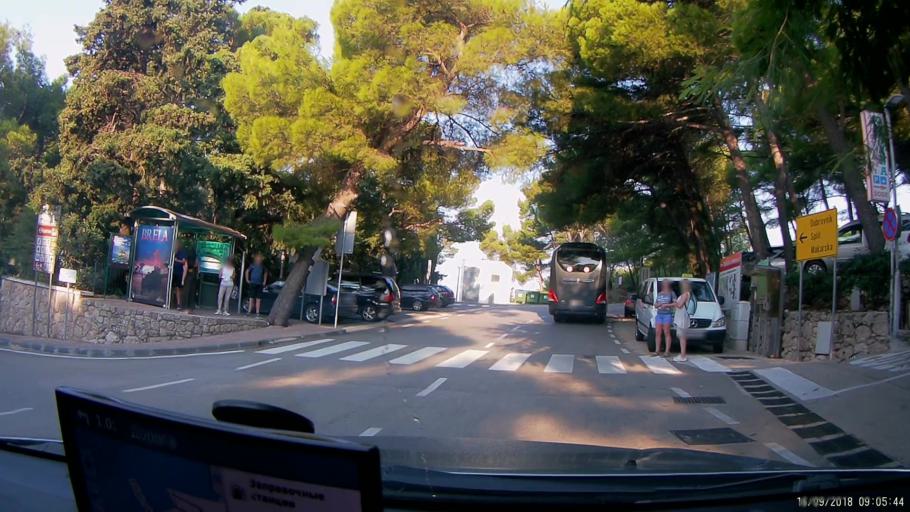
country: HR
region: Splitsko-Dalmatinska
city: Donja Brela
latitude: 43.3684
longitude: 16.9302
